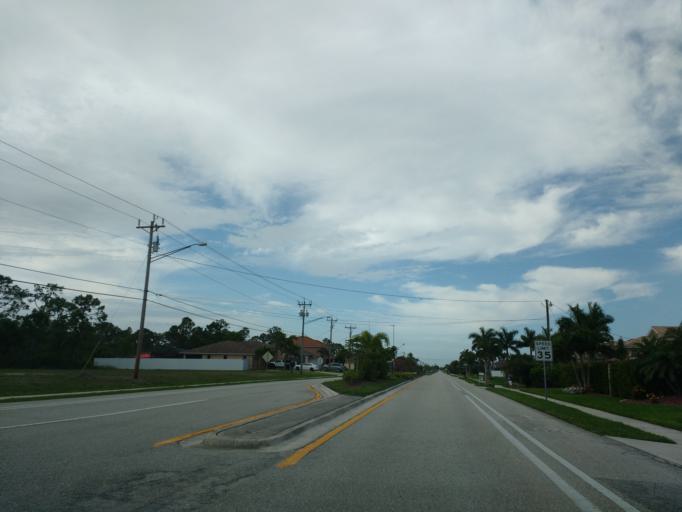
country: US
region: Florida
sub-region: Lee County
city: Cape Coral
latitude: 26.5852
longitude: -82.0240
